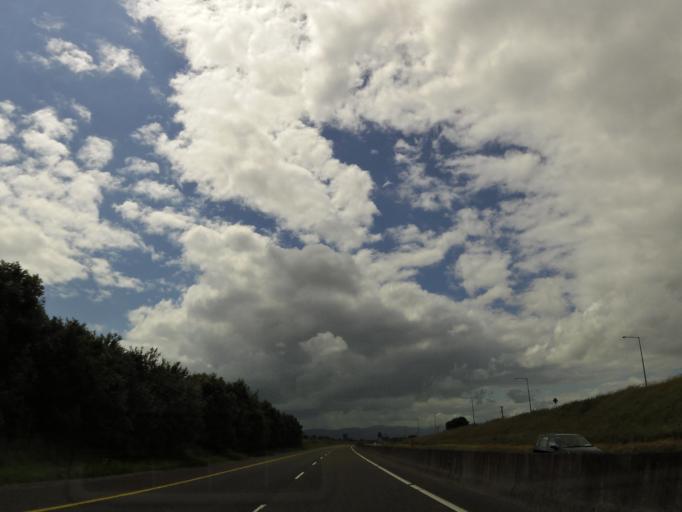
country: IE
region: Munster
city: Cashel
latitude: 52.5085
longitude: -7.8715
